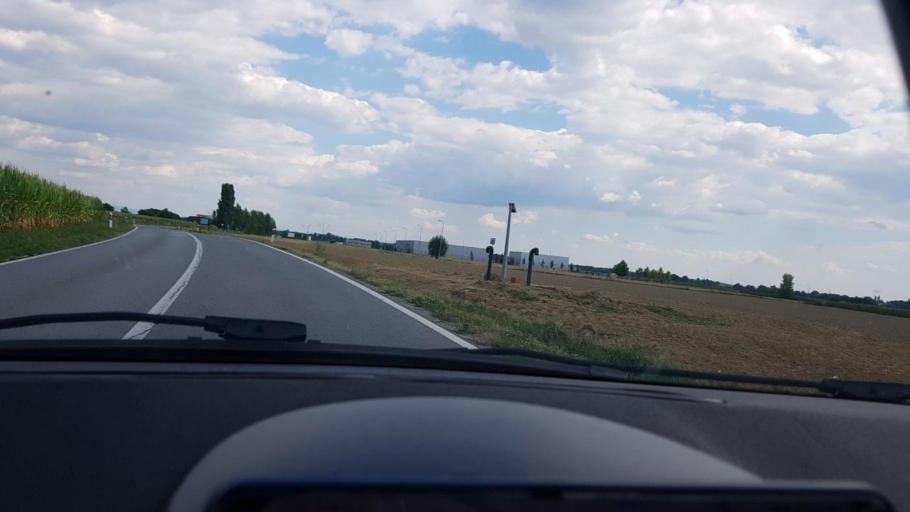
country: HR
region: Bjelovarsko-Bilogorska
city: Zdralovi
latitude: 45.8471
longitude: 16.9437
